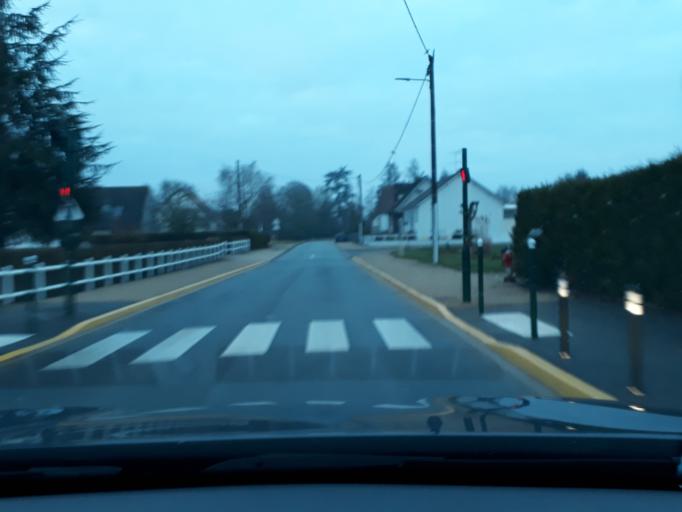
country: FR
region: Centre
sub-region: Departement du Loiret
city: Loury
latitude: 47.9995
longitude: 2.0844
